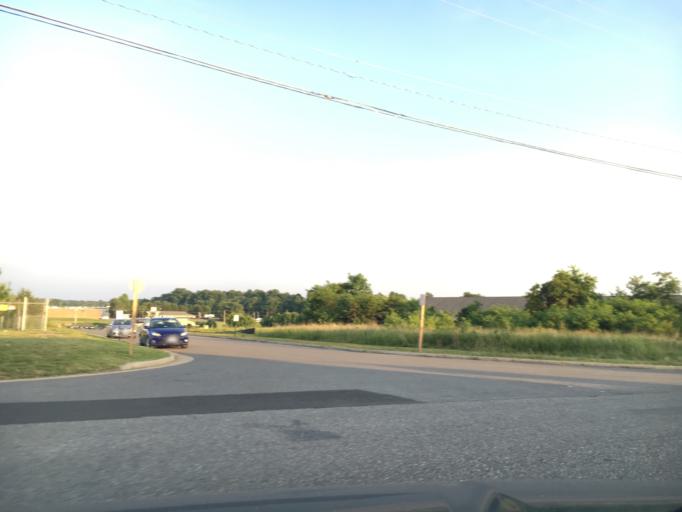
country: US
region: Virginia
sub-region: Bedford County
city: Forest
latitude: 37.3686
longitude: -79.3012
